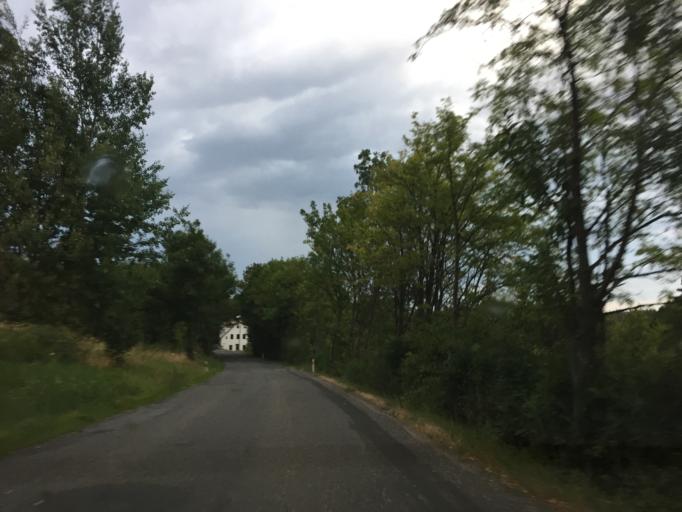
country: CZ
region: Liberecky
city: Mala Skala
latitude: 50.6655
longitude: 15.1876
